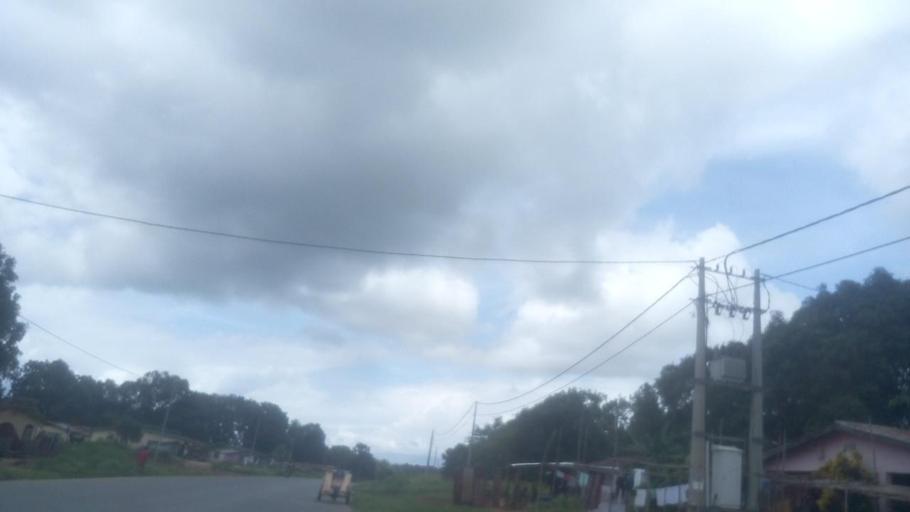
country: SL
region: Northern Province
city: Masoyila
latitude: 8.5877
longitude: -13.1647
